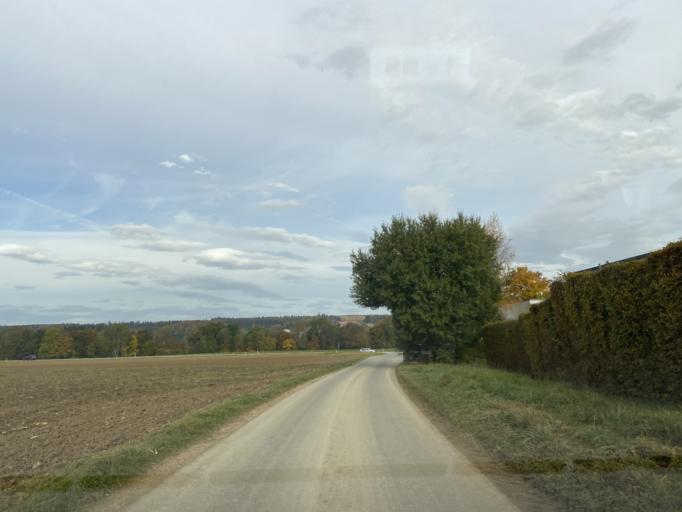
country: DE
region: Baden-Wuerttemberg
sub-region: Tuebingen Region
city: Bingen
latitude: 48.1048
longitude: 9.2646
